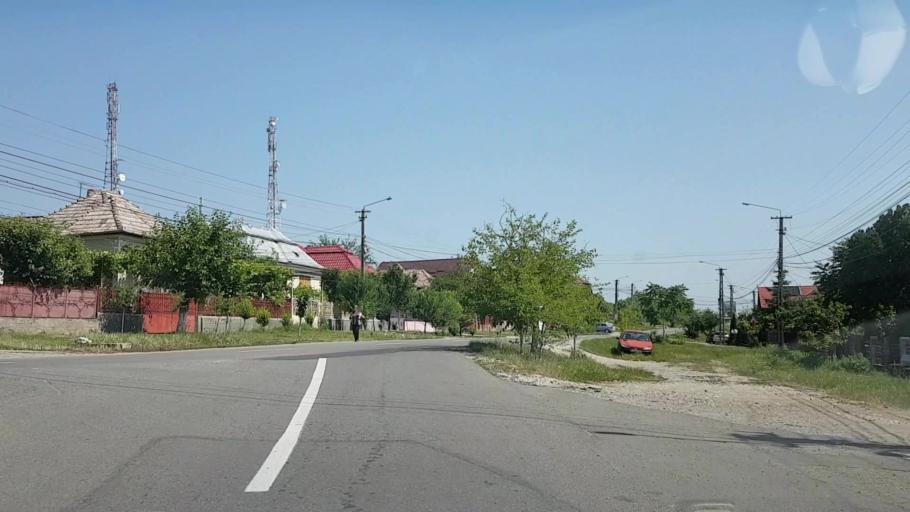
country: RO
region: Cluj
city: Turda
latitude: 46.5796
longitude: 23.7948
